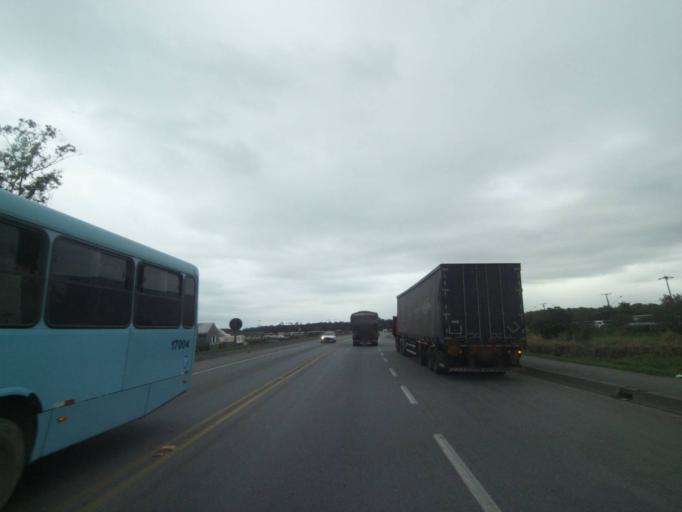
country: BR
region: Parana
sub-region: Paranagua
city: Paranagua
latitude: -25.5366
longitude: -48.5564
